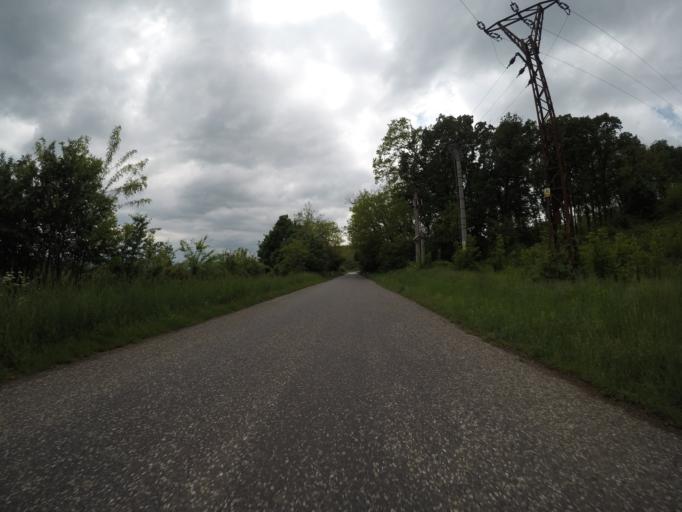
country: SK
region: Nitriansky
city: Sahy
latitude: 48.0907
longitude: 18.8692
